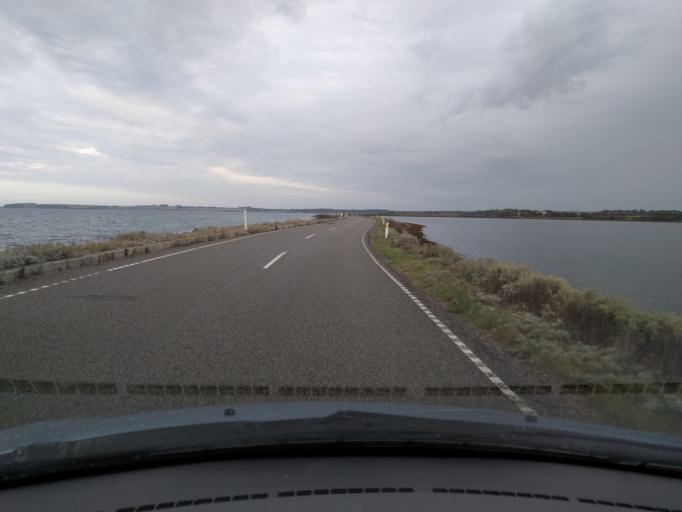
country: DK
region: South Denmark
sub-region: Assens Kommune
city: Assens
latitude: 55.1806
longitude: 9.9856
